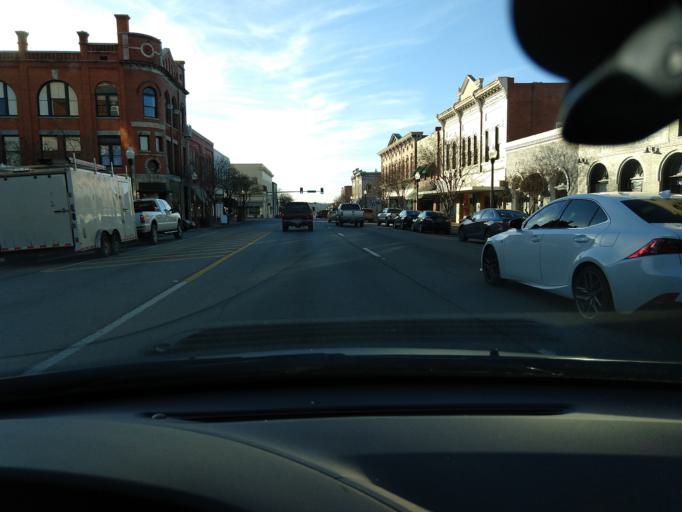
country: US
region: Georgia
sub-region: Sumter County
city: Americus
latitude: 32.0733
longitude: -84.2328
